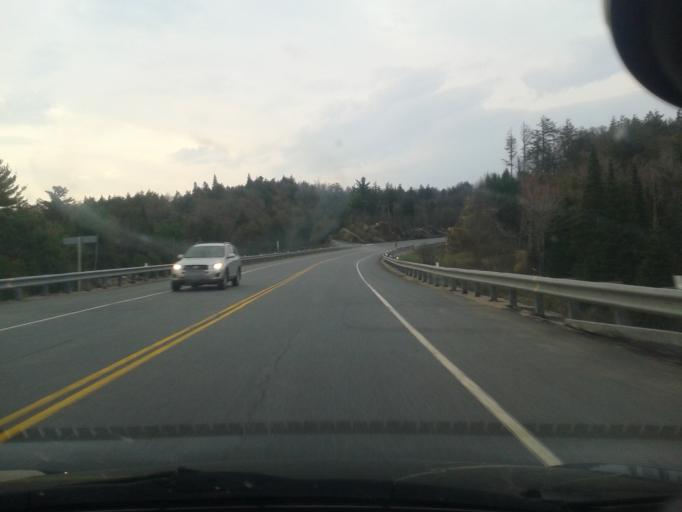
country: CA
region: Ontario
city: Huntsville
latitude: 45.5158
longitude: -78.7175
